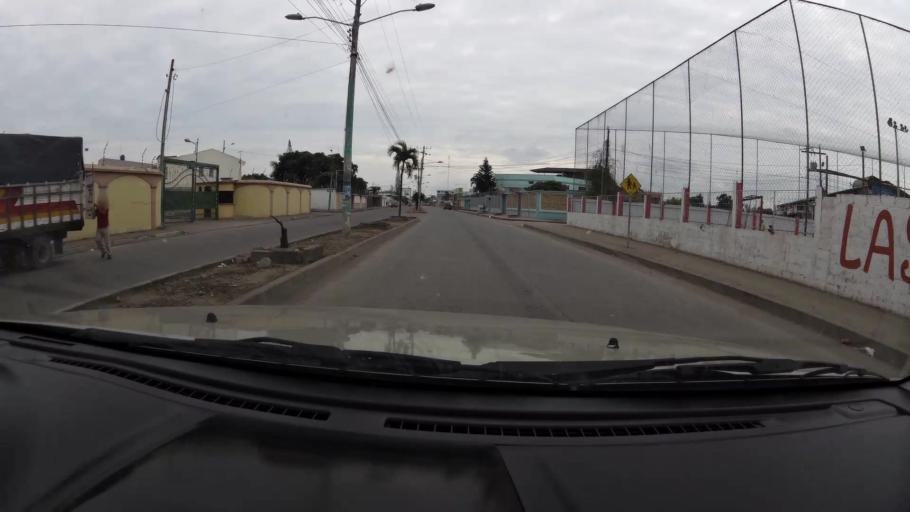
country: EC
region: El Oro
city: Machala
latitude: -3.2479
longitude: -79.9558
